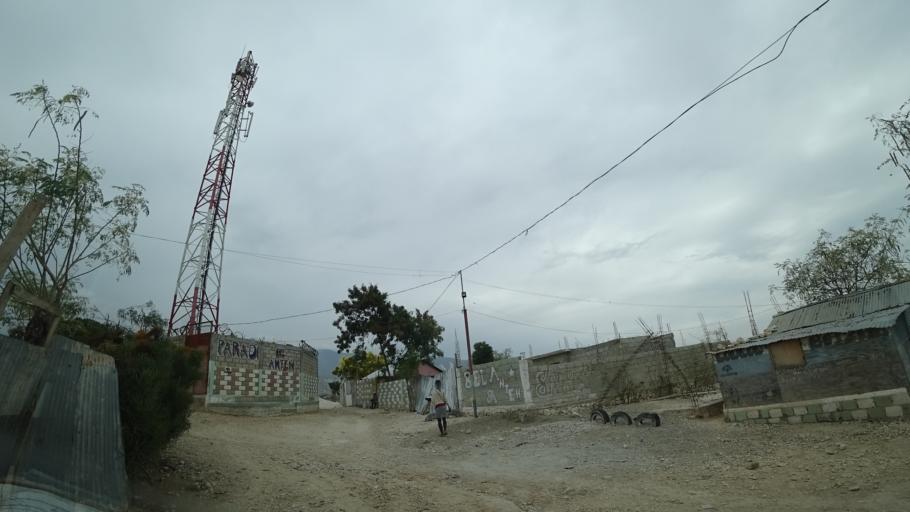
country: HT
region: Ouest
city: Croix des Bouquets
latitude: 18.6554
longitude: -72.2661
